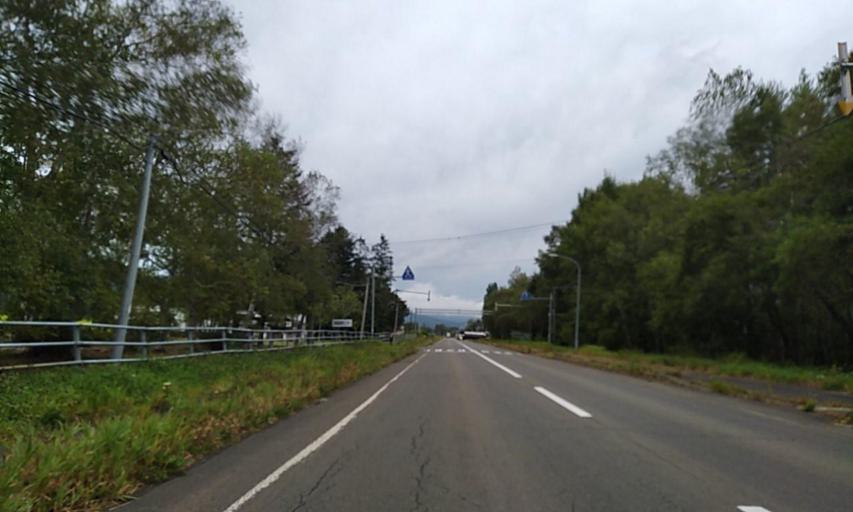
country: JP
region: Hokkaido
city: Bihoro
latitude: 43.5586
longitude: 144.3220
